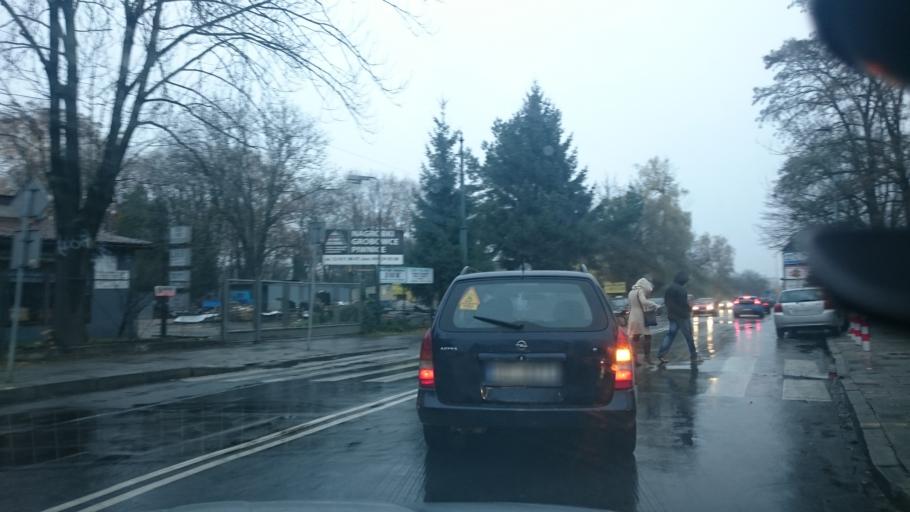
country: PL
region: Lesser Poland Voivodeship
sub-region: Krakow
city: Krakow
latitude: 50.0744
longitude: 19.9574
